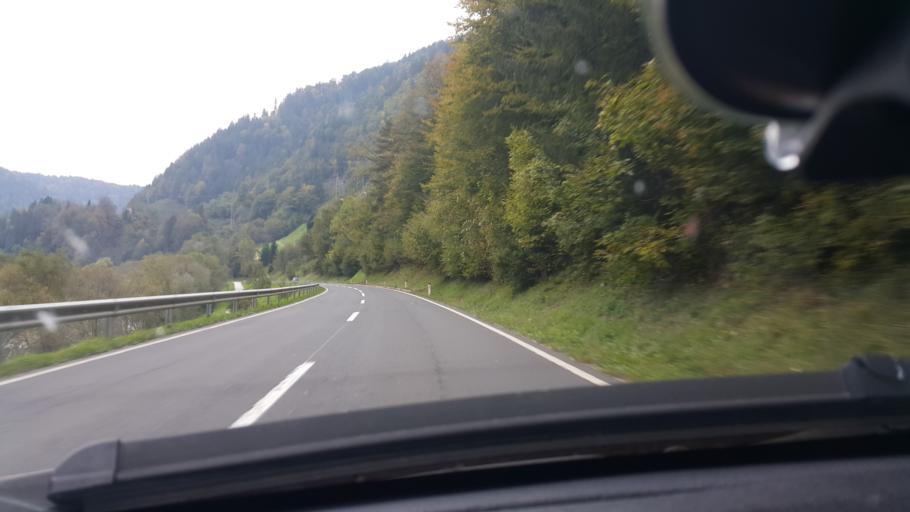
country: SI
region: Podvelka
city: Podvelka
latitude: 46.5938
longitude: 15.3372
